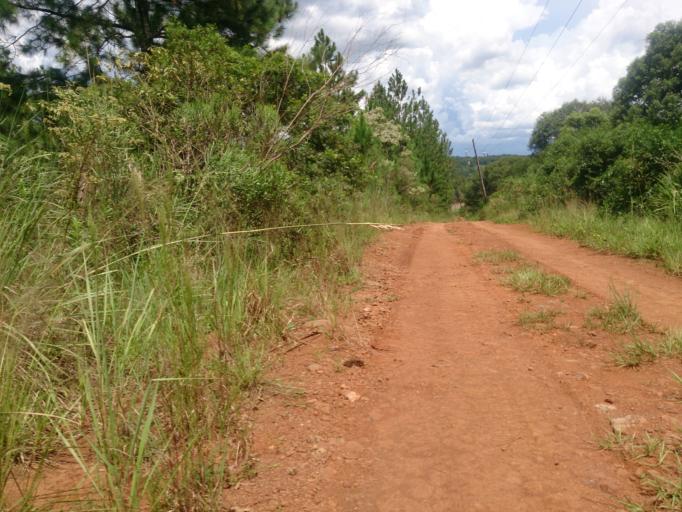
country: AR
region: Misiones
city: Campo Viera
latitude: -27.3632
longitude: -55.0494
